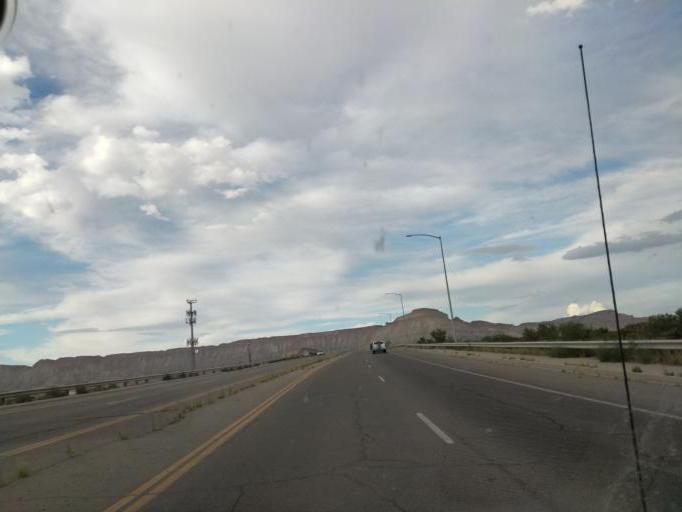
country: US
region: Colorado
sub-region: Mesa County
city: Clifton
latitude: 39.0843
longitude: -108.4584
